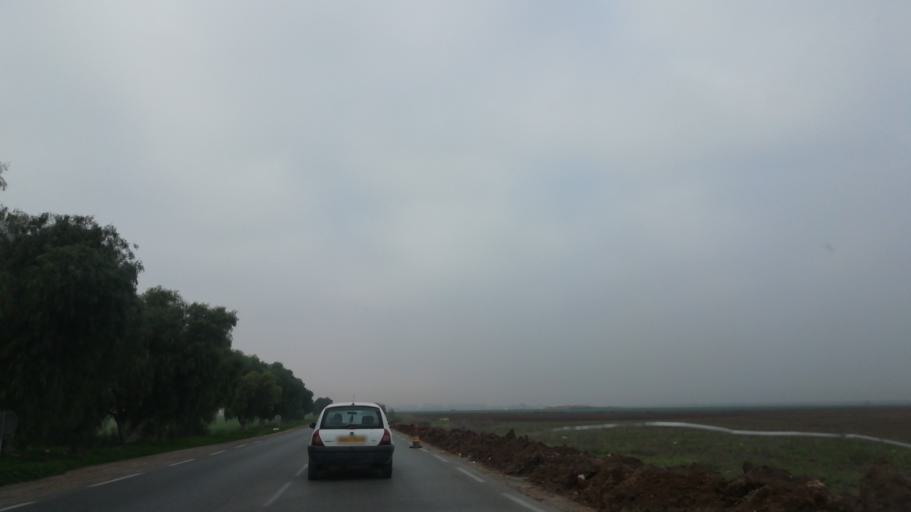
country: DZ
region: Relizane
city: Djidiouia
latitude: 35.9004
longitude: 0.7637
